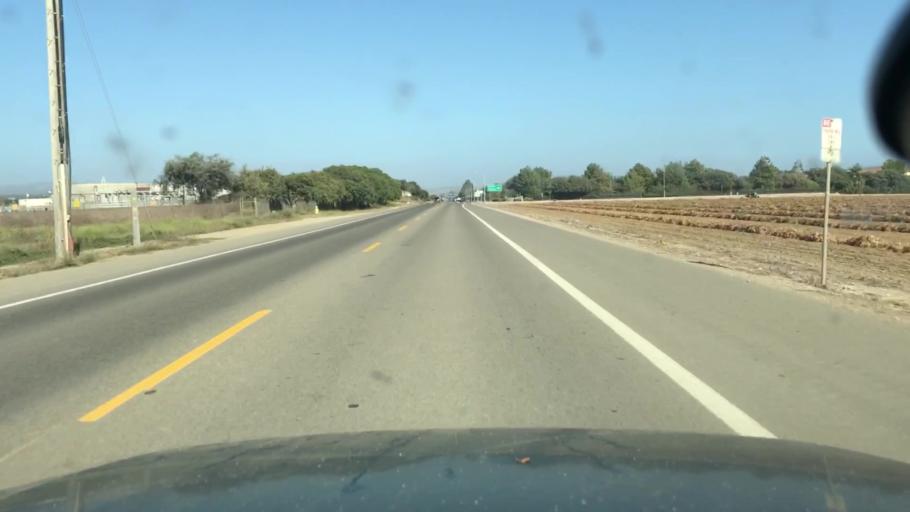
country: US
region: California
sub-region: Santa Barbara County
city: Lompoc
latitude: 34.6611
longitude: -120.4865
